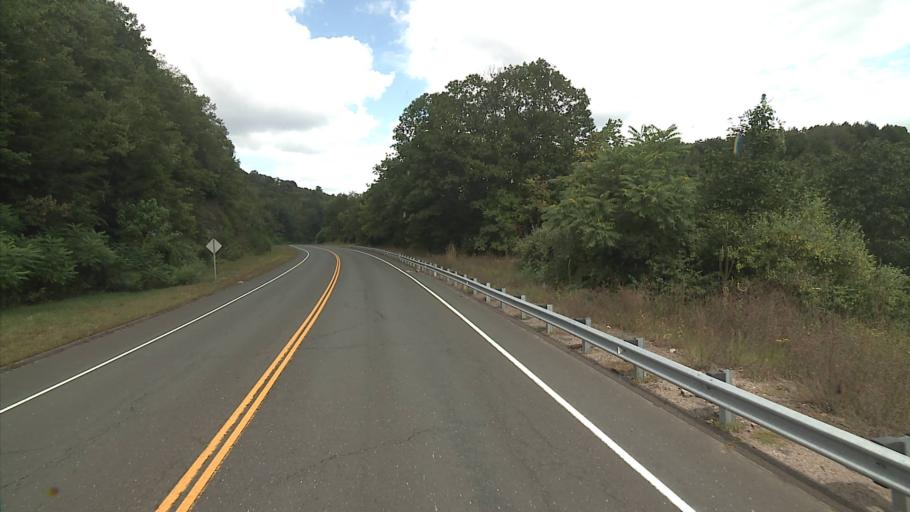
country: US
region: Connecticut
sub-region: Hartford County
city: Tariffville
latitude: 41.9008
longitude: -72.7575
